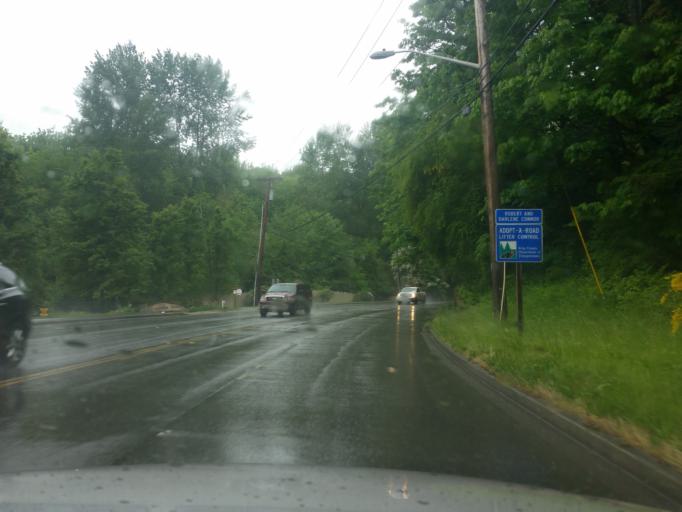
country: US
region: Washington
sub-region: King County
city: Inglewood-Finn Hill
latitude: 47.7309
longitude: -122.2094
